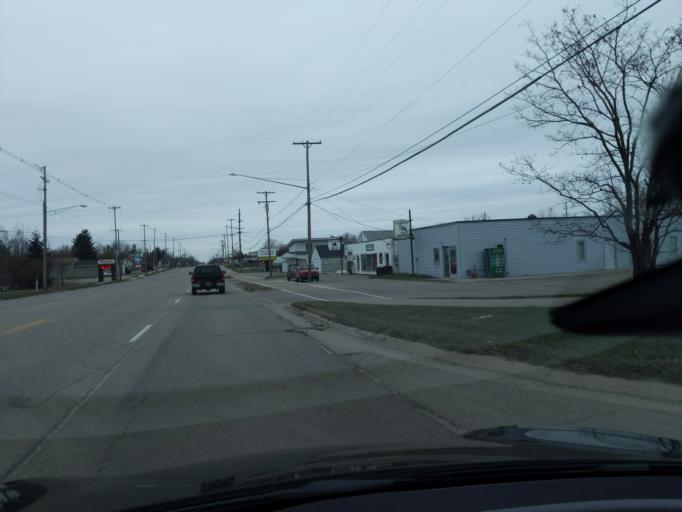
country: US
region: Michigan
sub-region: Ingham County
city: Lansing
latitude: 42.7758
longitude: -84.5426
